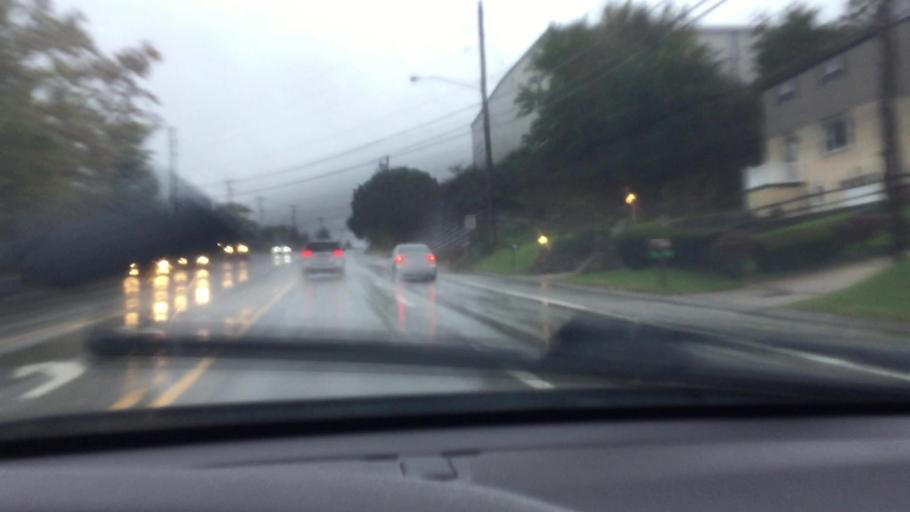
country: US
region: Pennsylvania
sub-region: Allegheny County
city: Pleasant Hills
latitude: 40.3334
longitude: -79.9347
